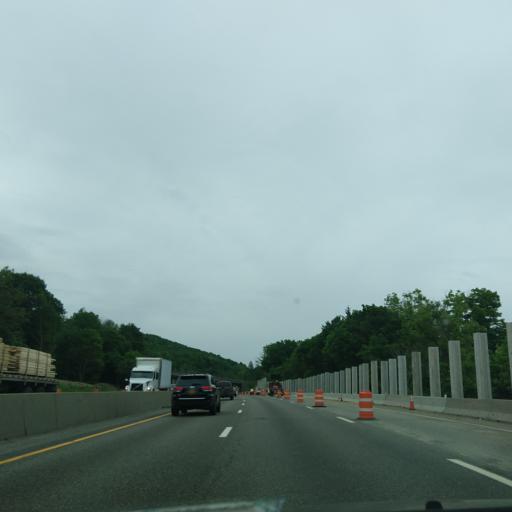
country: US
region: New York
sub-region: Broome County
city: Port Dickinson
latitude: 42.1136
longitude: -75.8800
